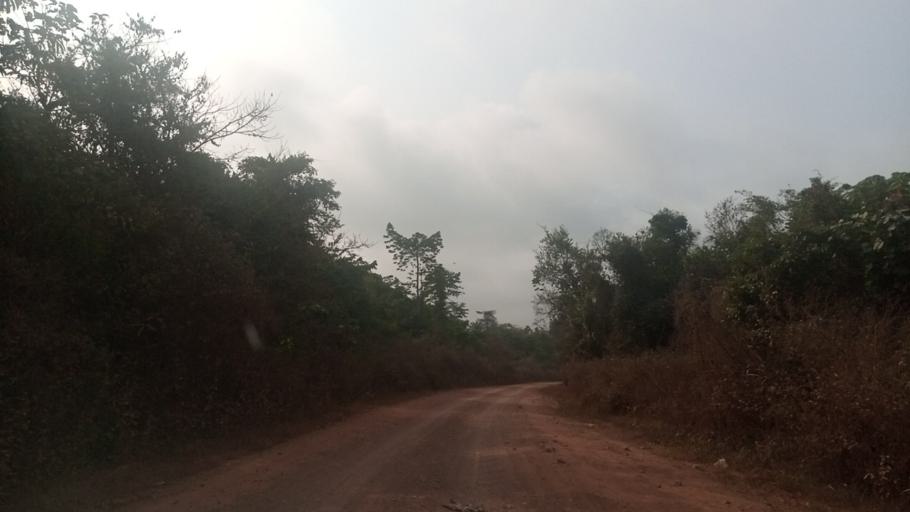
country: NG
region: Osun
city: Modakeke
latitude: 7.1245
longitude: 4.4085
